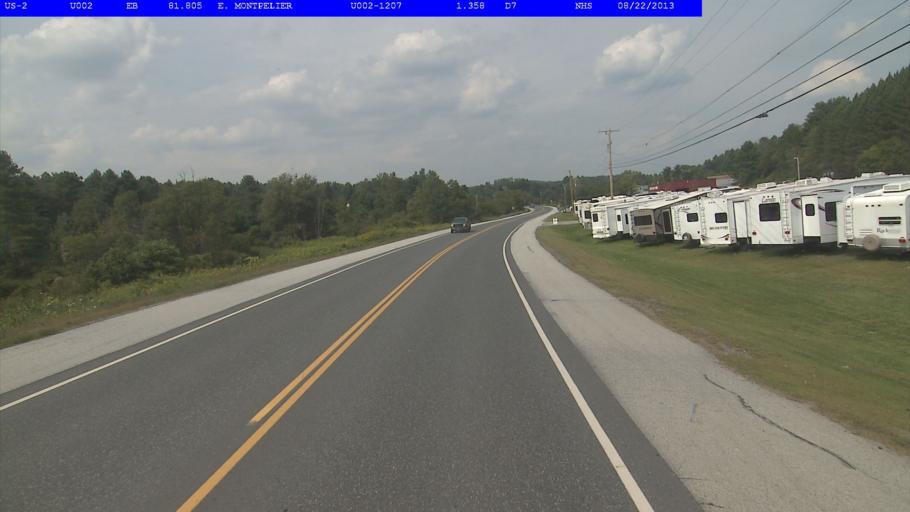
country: US
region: Vermont
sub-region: Washington County
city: Barre
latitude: 44.2527
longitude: -72.5020
